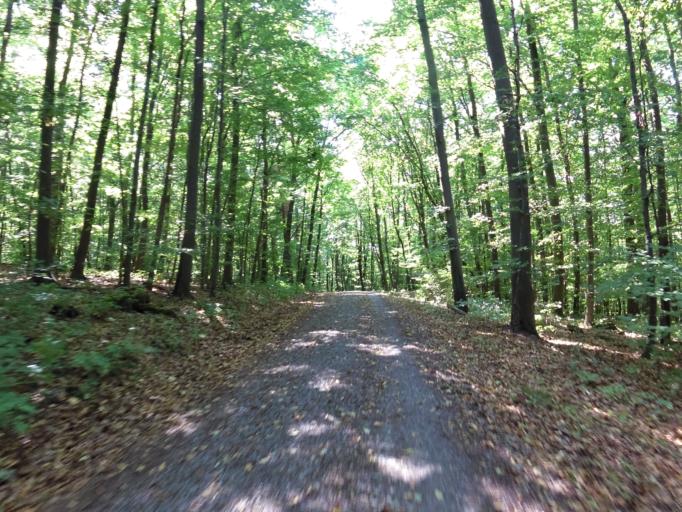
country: DE
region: Bavaria
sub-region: Regierungsbezirk Unterfranken
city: Wuerzburg
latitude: 49.7674
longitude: 9.8986
